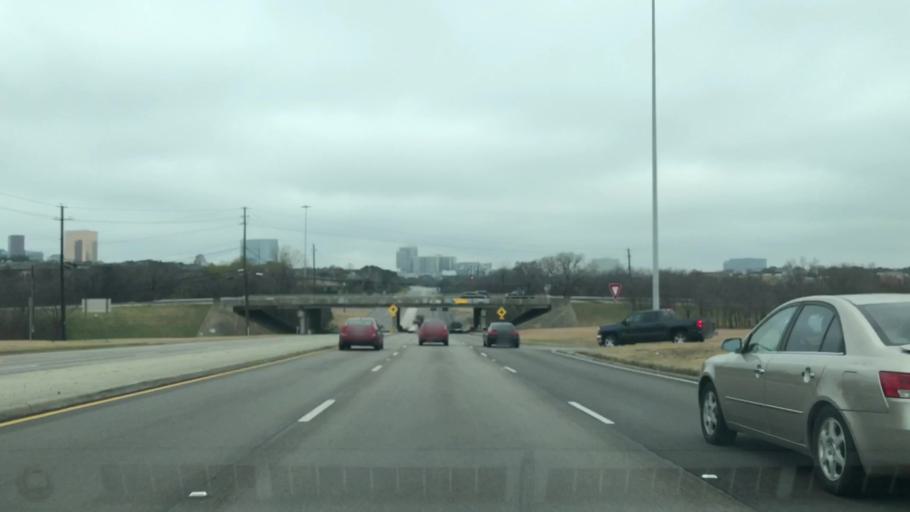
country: US
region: Texas
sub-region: Dallas County
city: Highland Park
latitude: 32.8586
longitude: -96.7525
